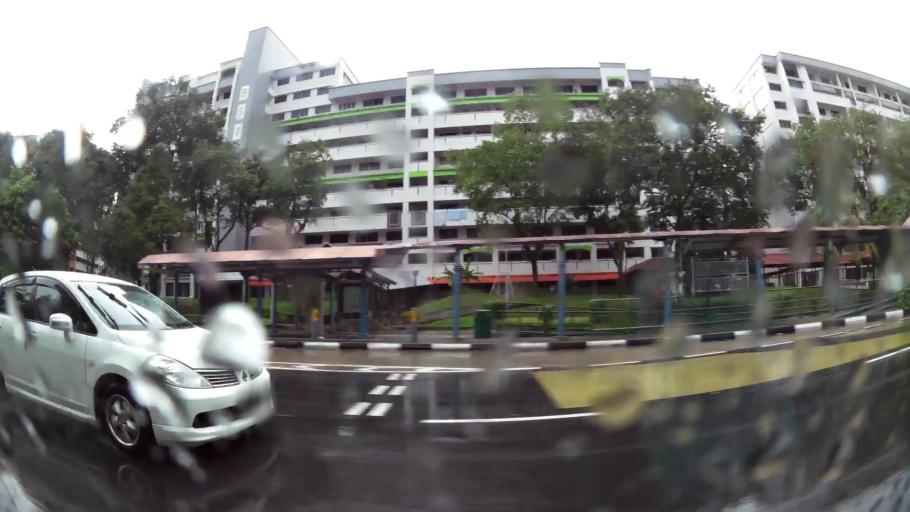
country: MY
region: Johor
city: Kampung Pasir Gudang Baru
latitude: 1.3804
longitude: 103.8905
